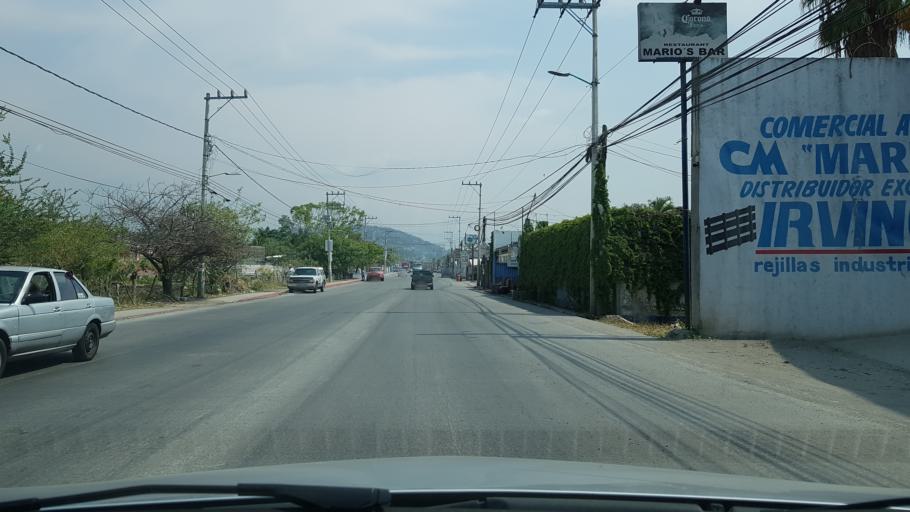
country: MX
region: Morelos
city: Emiliano Zapata
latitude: 18.8246
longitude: -99.1890
